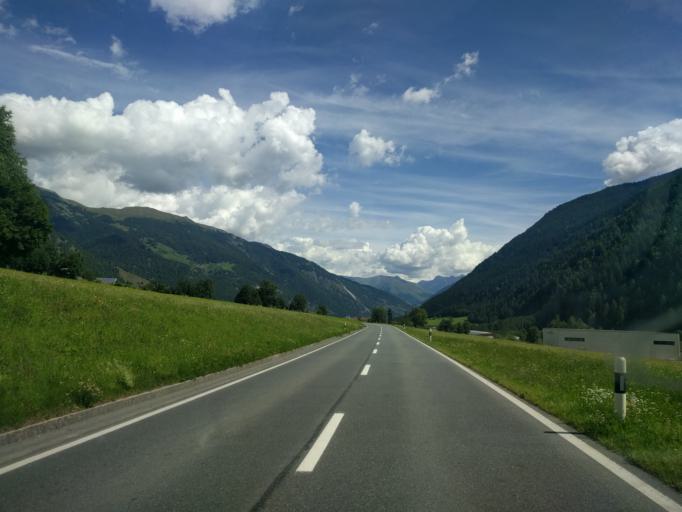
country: IT
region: Trentino-Alto Adige
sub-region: Bolzano
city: Tubre
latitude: 46.6162
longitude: 10.4428
